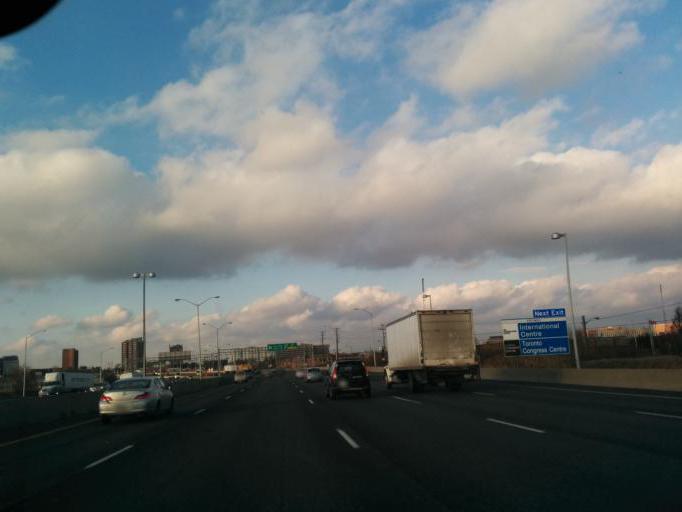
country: CA
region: Ontario
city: Etobicoke
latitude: 43.6779
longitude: -79.5924
